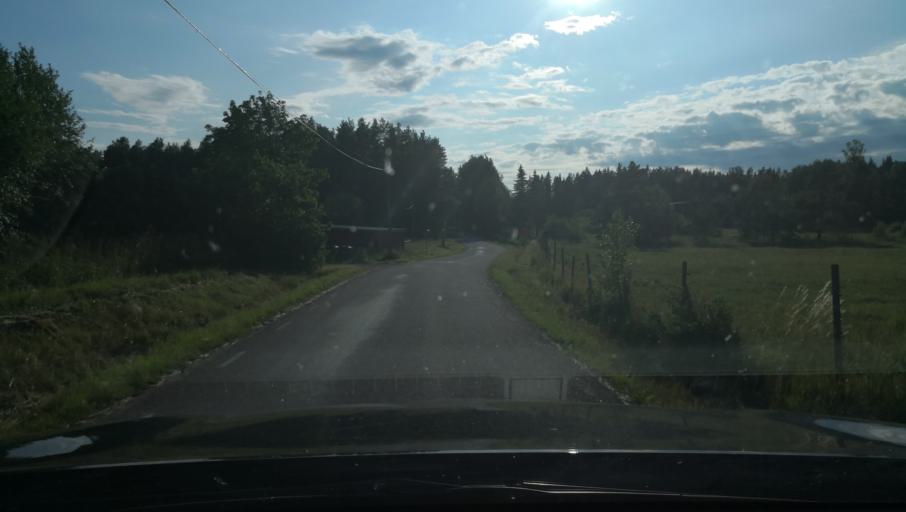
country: SE
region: Uppsala
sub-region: Osthammars Kommun
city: Osterbybruk
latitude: 60.0205
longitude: 17.9547
